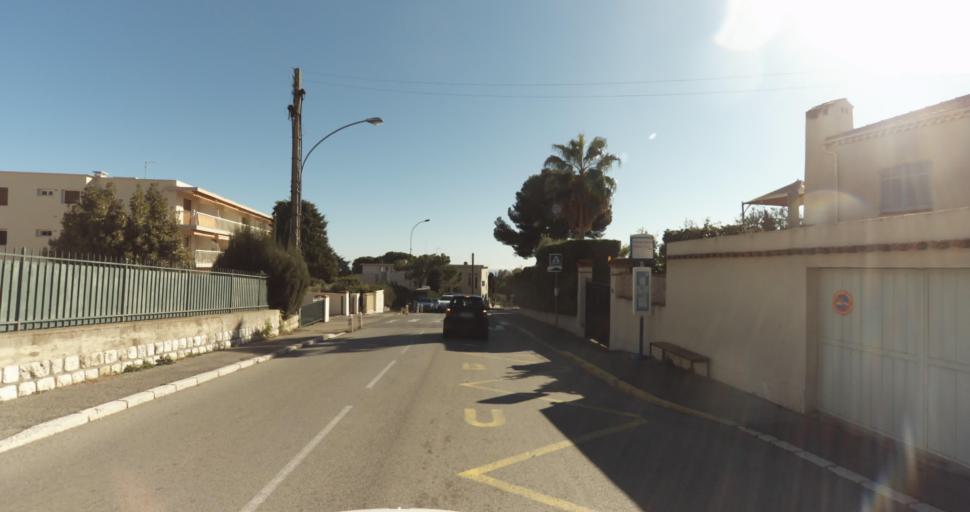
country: FR
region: Provence-Alpes-Cote d'Azur
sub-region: Departement des Alpes-Maritimes
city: Vence
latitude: 43.7185
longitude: 7.1186
